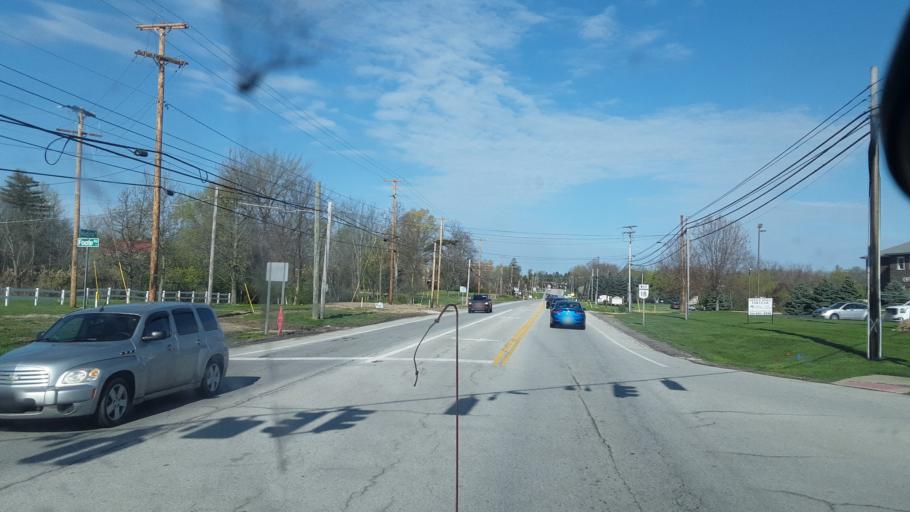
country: US
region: Ohio
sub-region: Medina County
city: Medina
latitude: 41.1382
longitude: -81.8315
